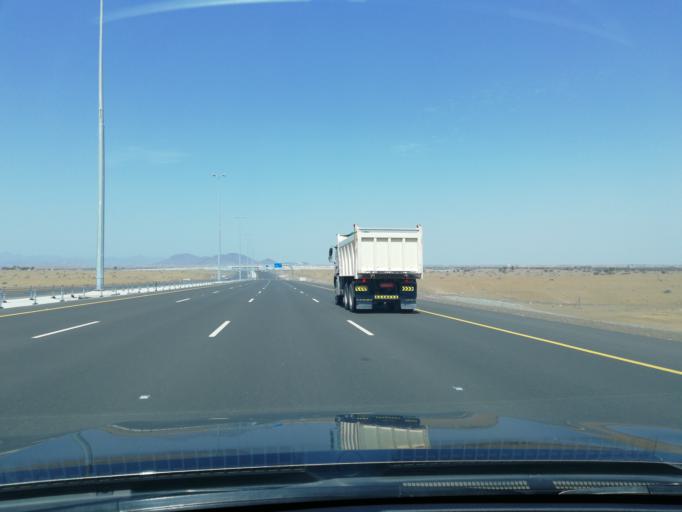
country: OM
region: Al Batinah
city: Rustaq
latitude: 23.5332
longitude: 57.5760
